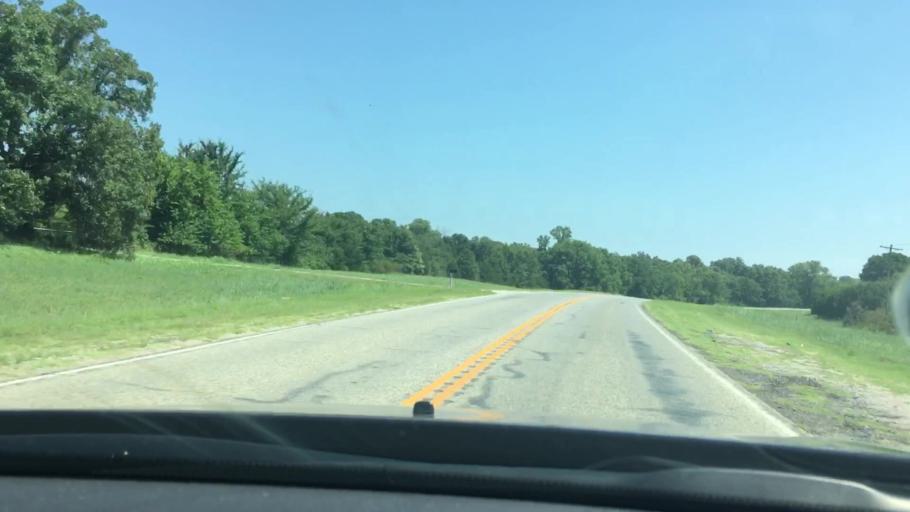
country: US
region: Oklahoma
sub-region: Johnston County
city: Tishomingo
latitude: 34.2358
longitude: -96.6153
